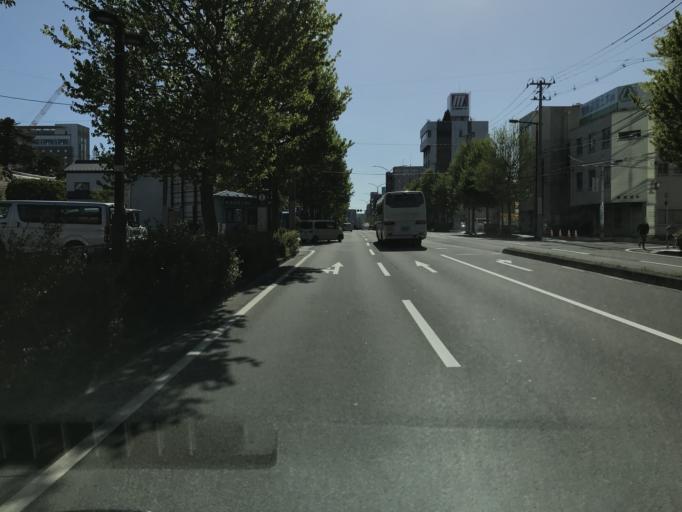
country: JP
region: Miyagi
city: Sendai-shi
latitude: 38.2560
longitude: 140.8880
